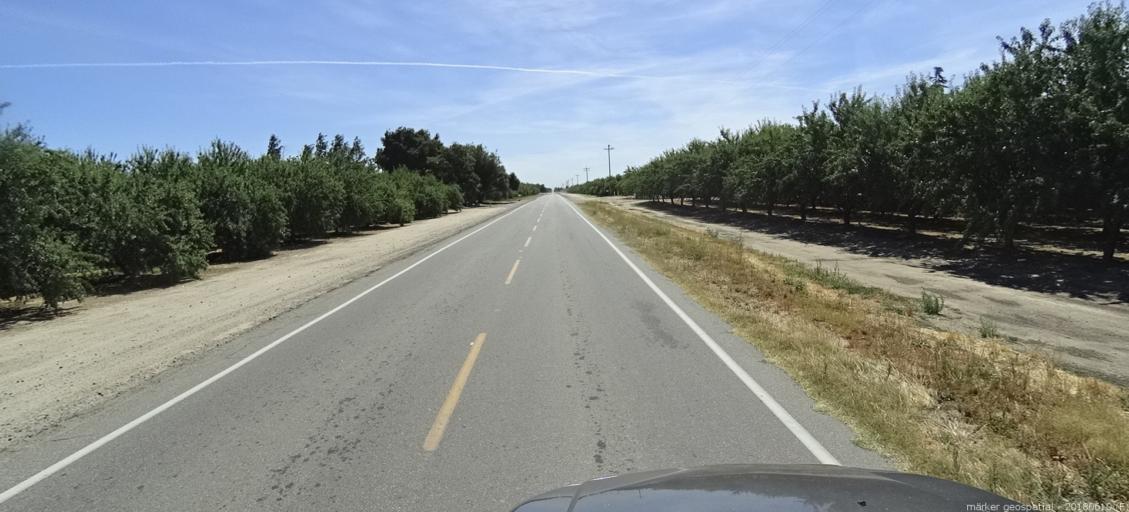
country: US
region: California
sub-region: Madera County
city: Chowchilla
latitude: 37.0181
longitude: -120.3618
